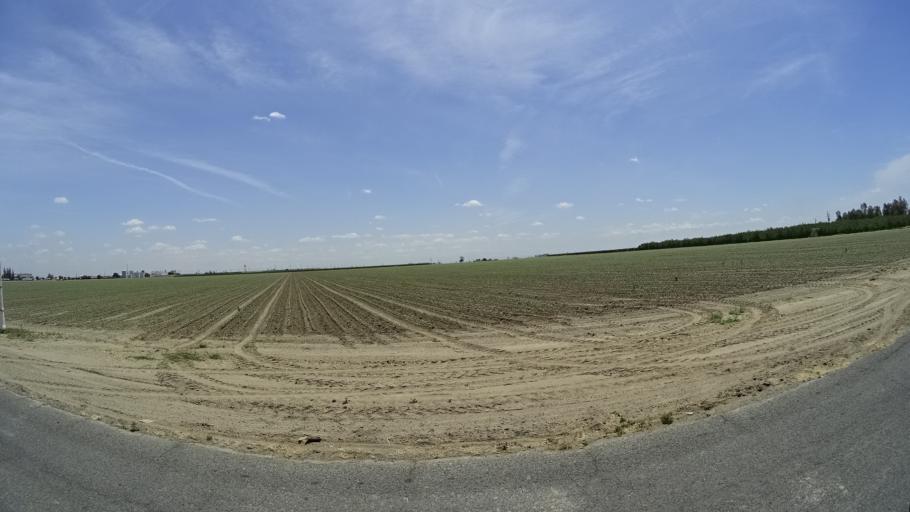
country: US
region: California
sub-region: Kings County
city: Home Garden
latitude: 36.2838
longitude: -119.6617
